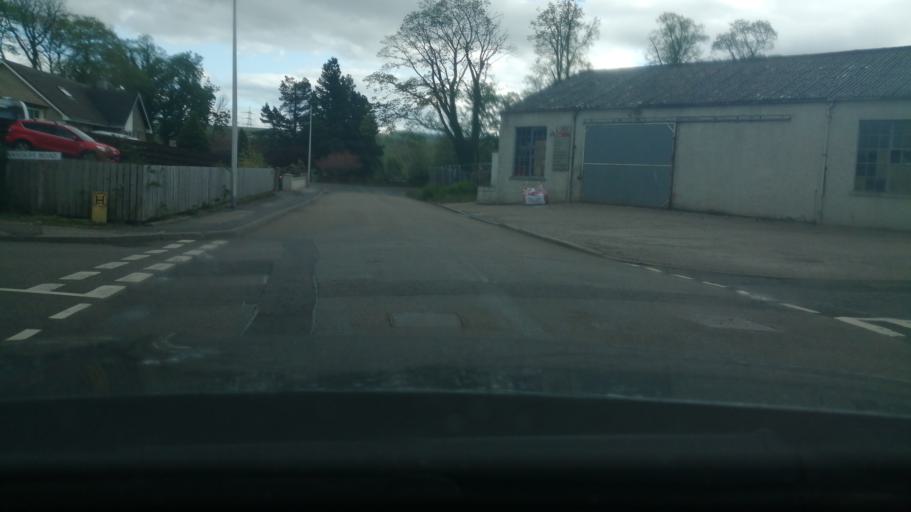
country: GB
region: Scotland
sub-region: Moray
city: Keith
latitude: 57.5365
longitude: -2.9480
